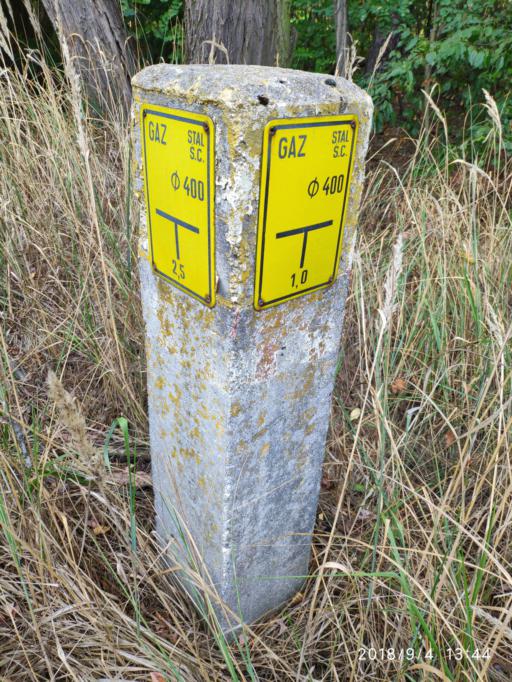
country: PL
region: Lubusz
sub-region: Zielona Gora
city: Zielona Gora
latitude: 51.9713
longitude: 15.5448
